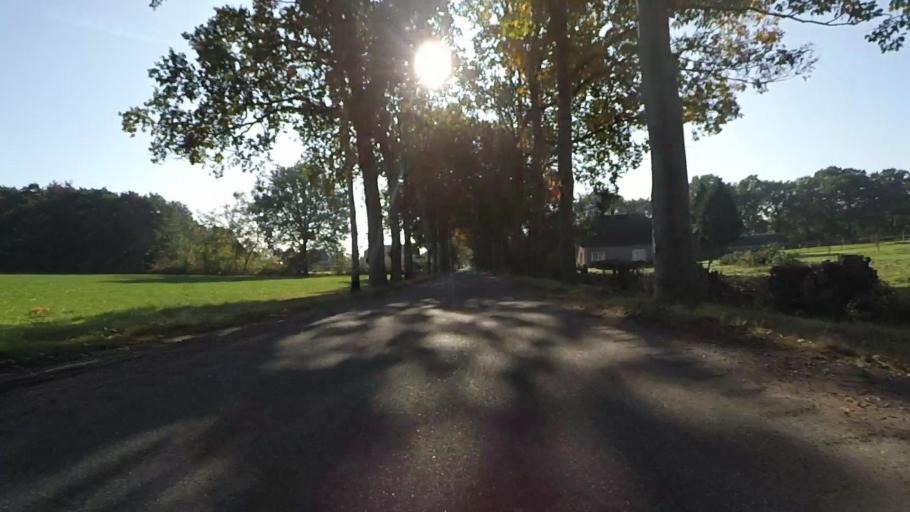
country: NL
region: Gelderland
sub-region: Gemeente Nijkerk
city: Nijkerk
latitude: 52.2195
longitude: 5.5287
